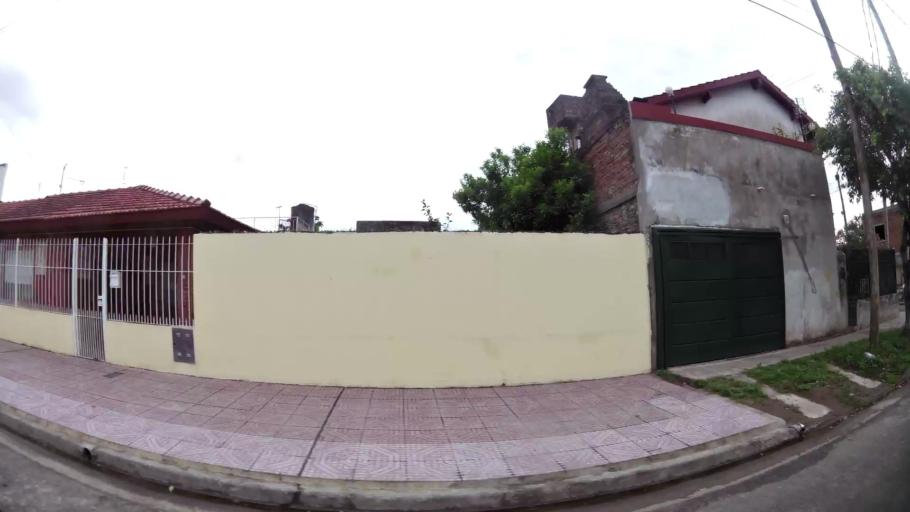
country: AR
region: Buenos Aires
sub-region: Partido de Lomas de Zamora
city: Lomas de Zamora
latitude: -34.7385
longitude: -58.3671
